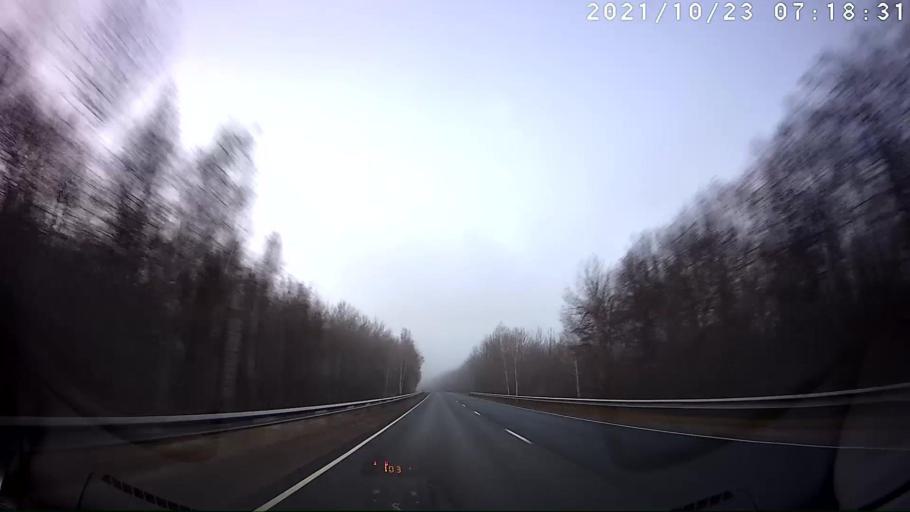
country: RU
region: Saratov
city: Khvalynsk
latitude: 52.4516
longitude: 48.0127
